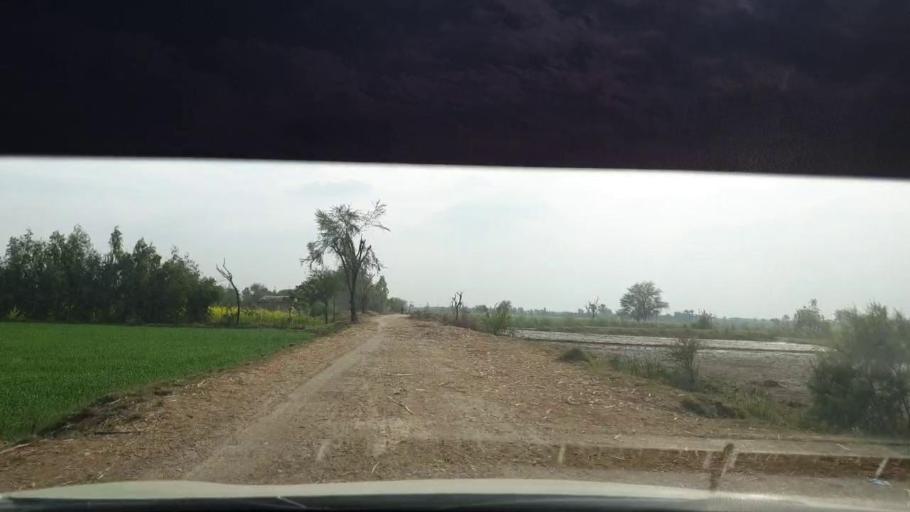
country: PK
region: Sindh
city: Berani
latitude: 25.7579
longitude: 68.8766
